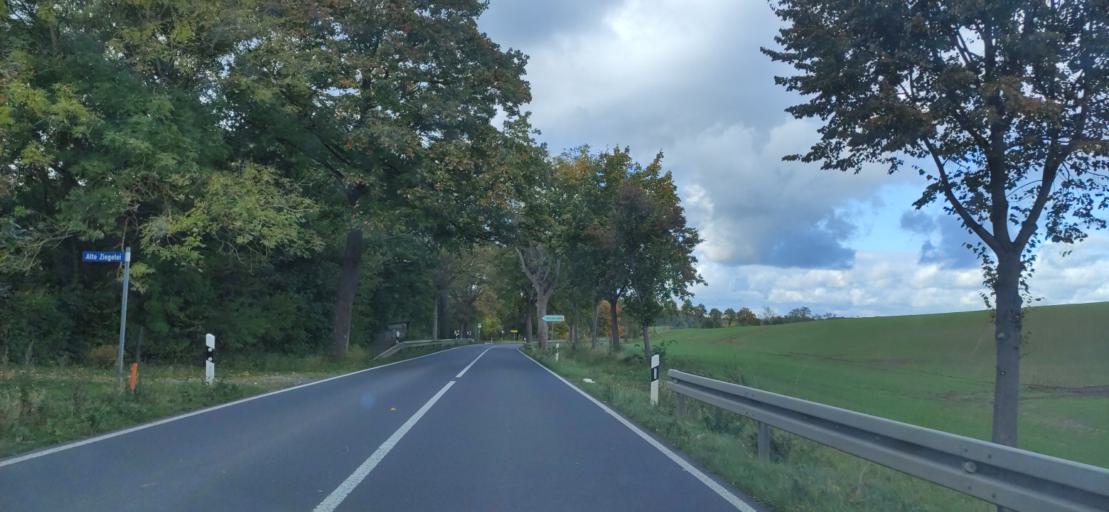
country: DE
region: Mecklenburg-Vorpommern
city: Grabowhofe
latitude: 53.6037
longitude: 12.6037
